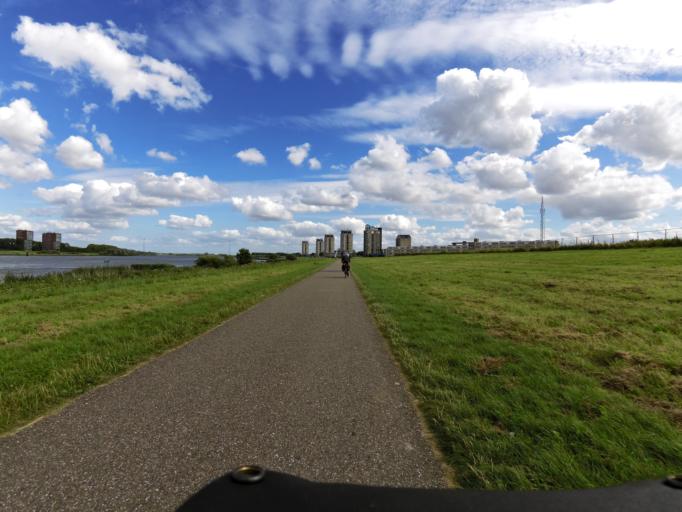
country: NL
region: South Holland
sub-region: Gemeente Spijkenisse
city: Spijkenisse
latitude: 51.8507
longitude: 4.3461
